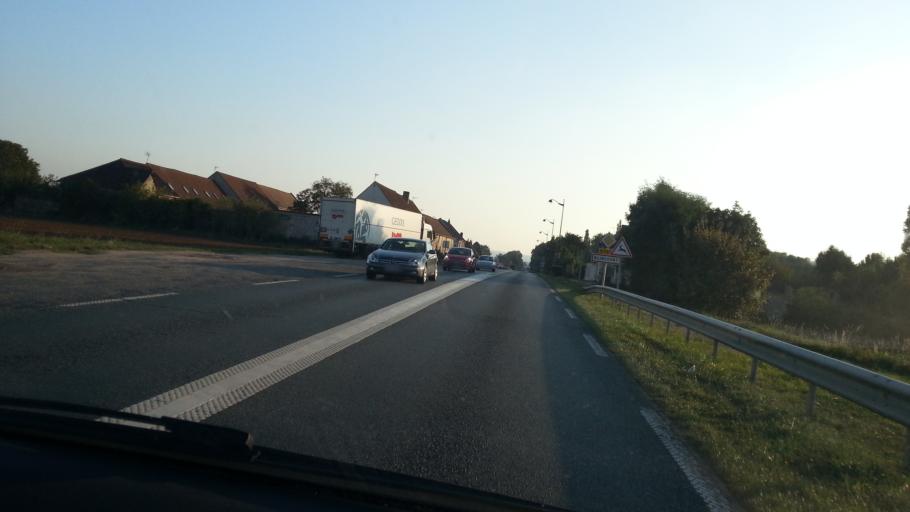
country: FR
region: Picardie
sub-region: Departement de l'Oise
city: Grandfresnoy
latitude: 49.3870
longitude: 2.6210
